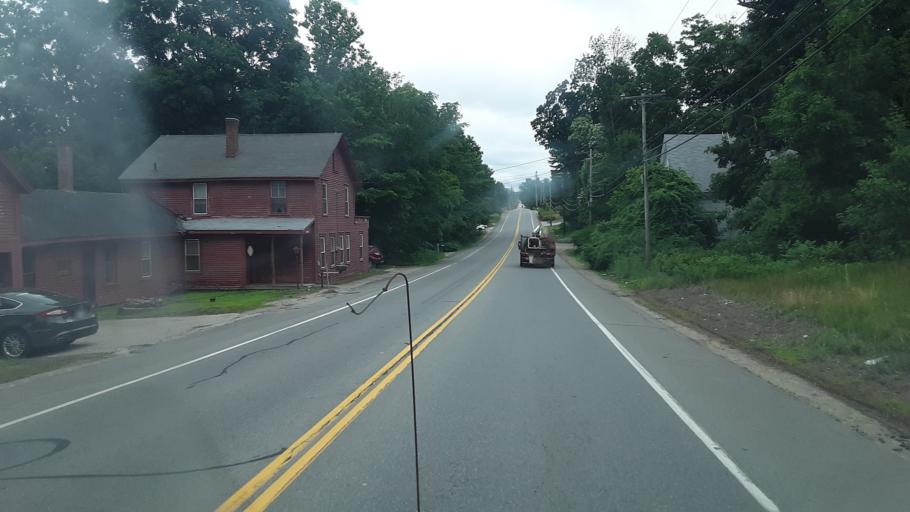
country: US
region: New Hampshire
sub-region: Rockingham County
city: Northwood
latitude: 43.1962
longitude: -71.1541
